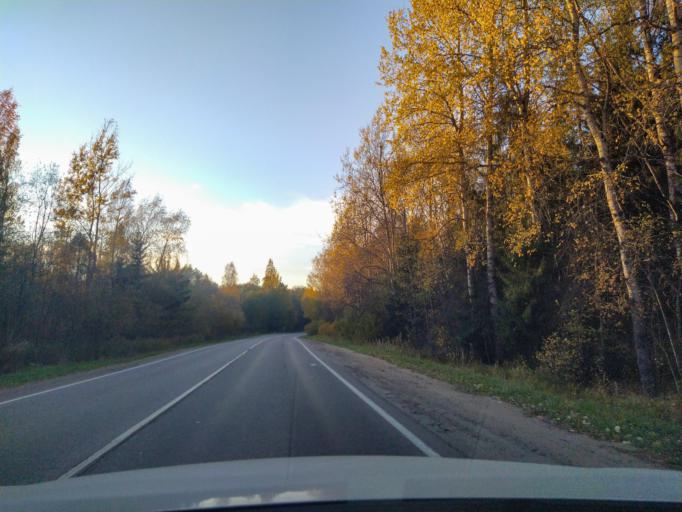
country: RU
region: Leningrad
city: Kobrinskoye
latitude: 59.4068
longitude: 30.1259
